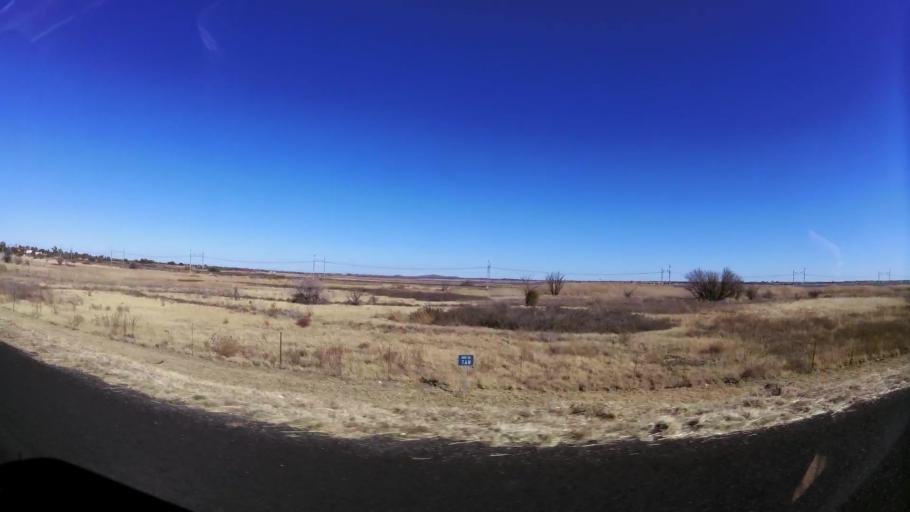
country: ZA
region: Northern Cape
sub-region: Frances Baard District Municipality
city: Kimberley
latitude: -28.6804
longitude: 24.7777
